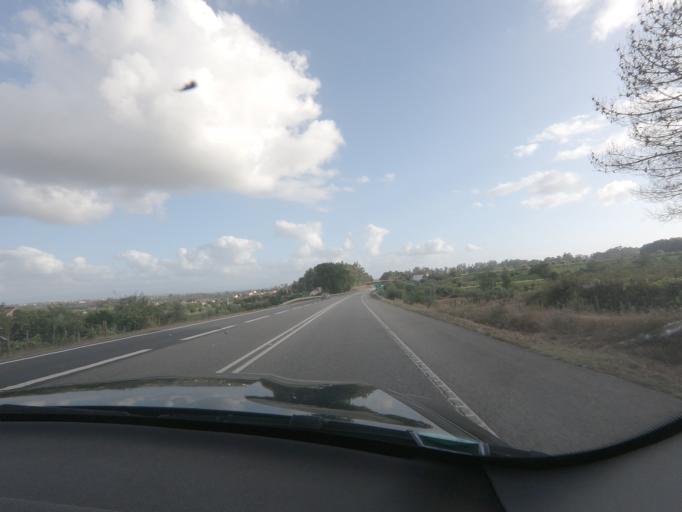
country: PT
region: Viseu
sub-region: Concelho de Tondela
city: Tondela
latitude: 40.5521
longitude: -8.0526
